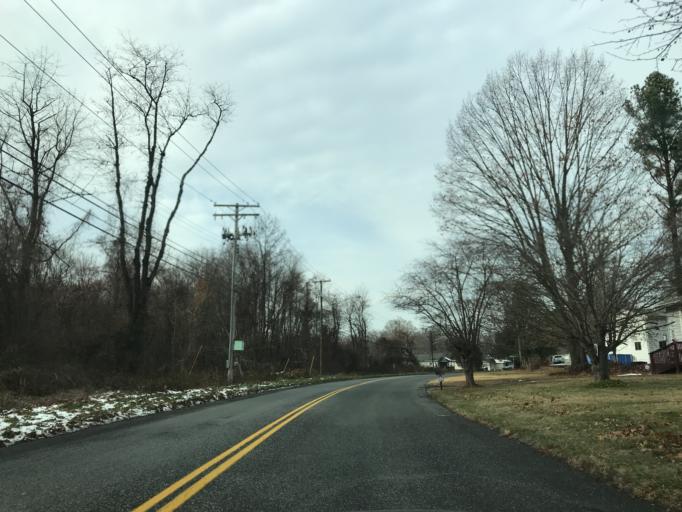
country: US
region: Maryland
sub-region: Harford County
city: Perryman
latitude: 39.4768
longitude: -76.2046
